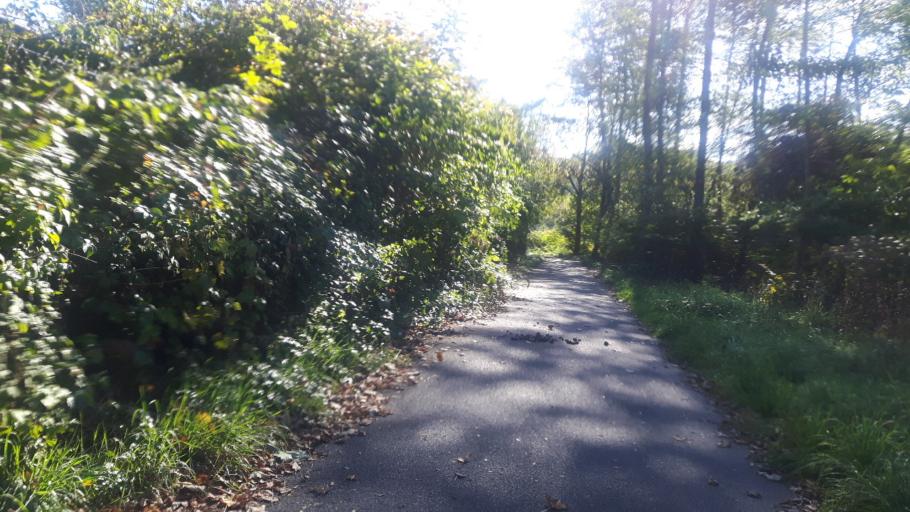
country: DE
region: Rheinland-Pfalz
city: Niederirsen
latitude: 50.7969
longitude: 7.6056
